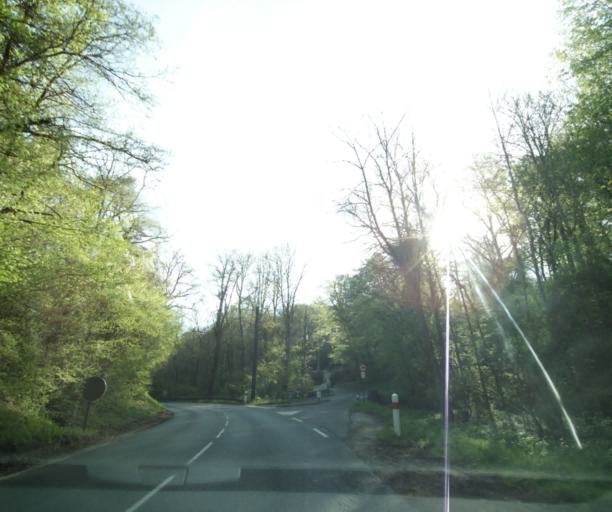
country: FR
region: Ile-de-France
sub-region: Departement de Seine-et-Marne
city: Saint-Mammes
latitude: 48.3973
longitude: 2.8292
